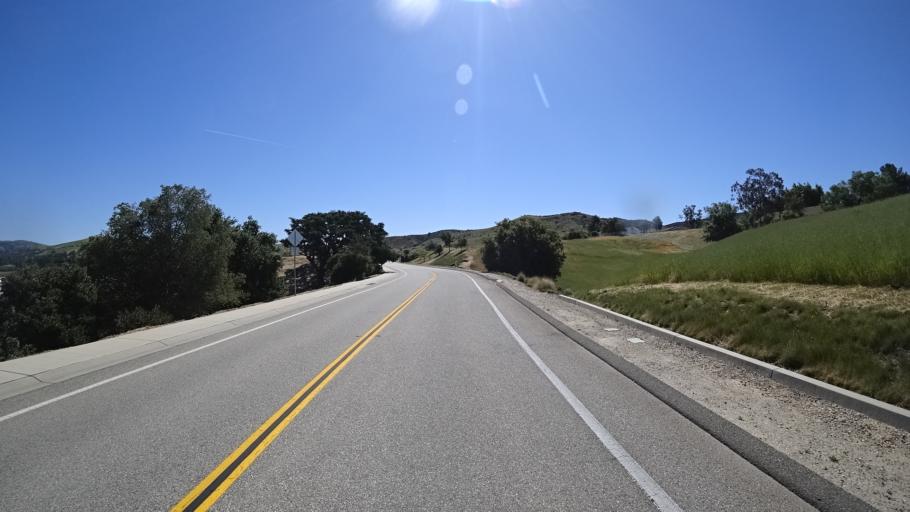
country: US
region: California
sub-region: Ventura County
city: Thousand Oaks
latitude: 34.1756
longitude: -118.8650
